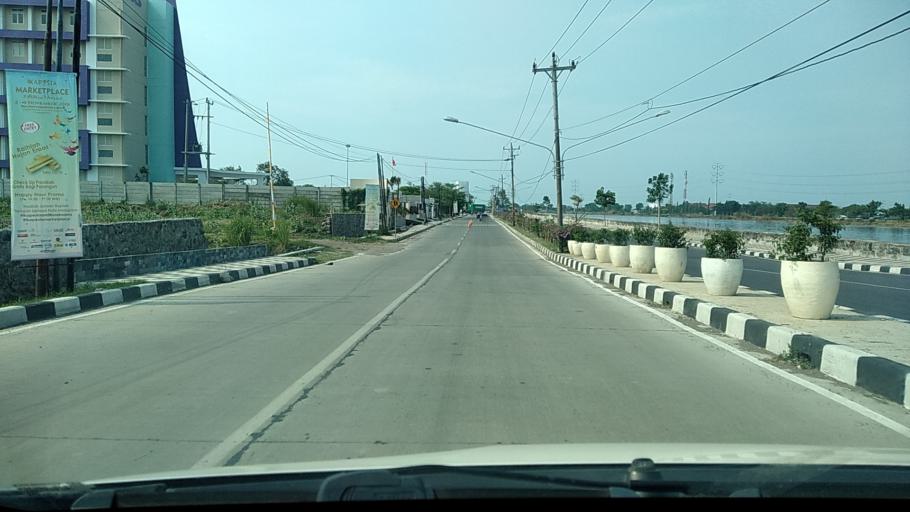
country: ID
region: Central Java
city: Semarang
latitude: -6.9644
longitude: 110.3994
